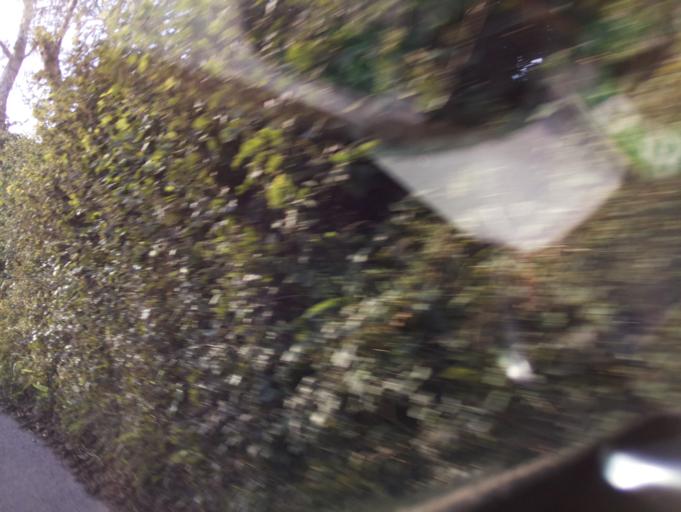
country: GB
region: England
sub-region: Devon
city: Totnes
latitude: 50.3459
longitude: -3.6754
